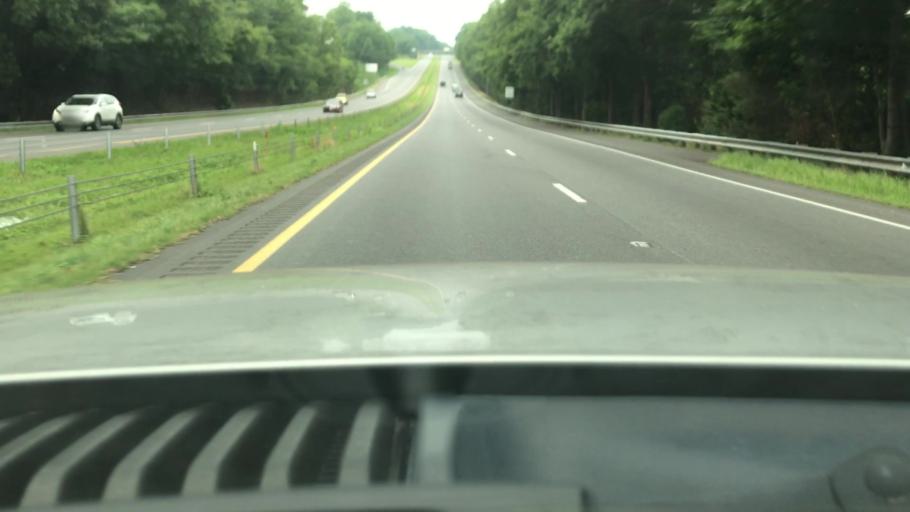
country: US
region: North Carolina
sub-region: Wilkes County
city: Wilkesboro
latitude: 36.1354
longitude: -81.1525
